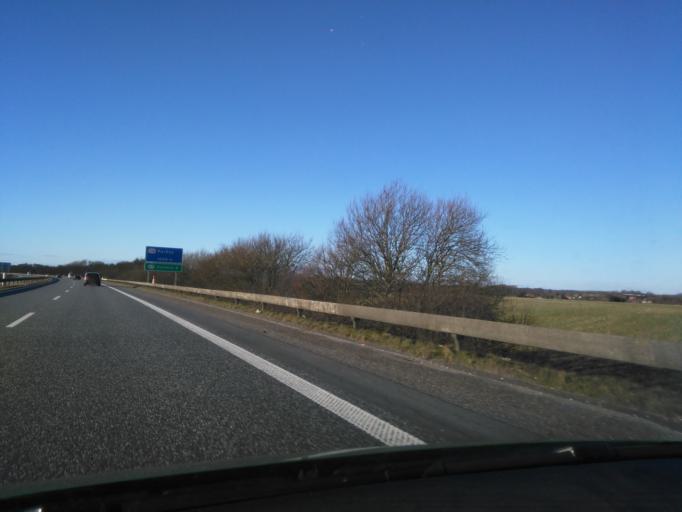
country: DK
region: Central Jutland
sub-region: Randers Kommune
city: Spentrup
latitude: 56.5354
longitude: 9.9233
